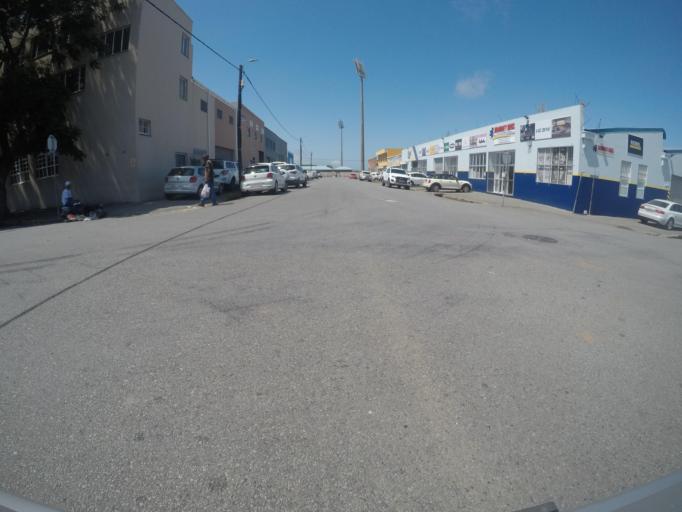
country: ZA
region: Eastern Cape
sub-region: Buffalo City Metropolitan Municipality
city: East London
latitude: -33.0083
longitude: 27.9045
